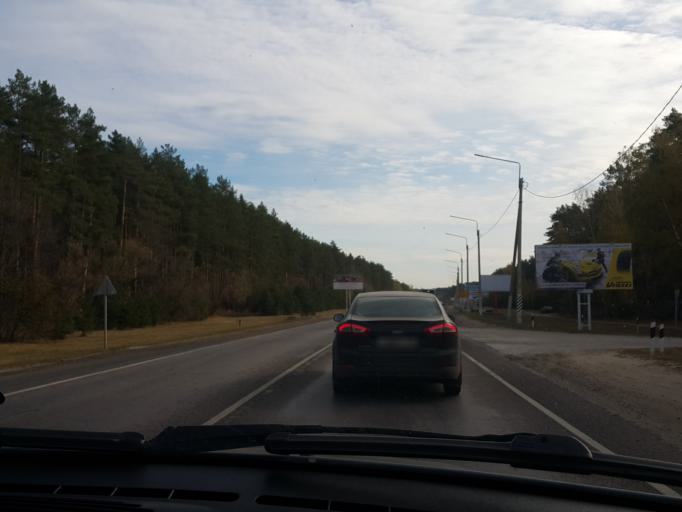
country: RU
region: Tambov
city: Donskoye
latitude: 52.7136
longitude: 41.5182
